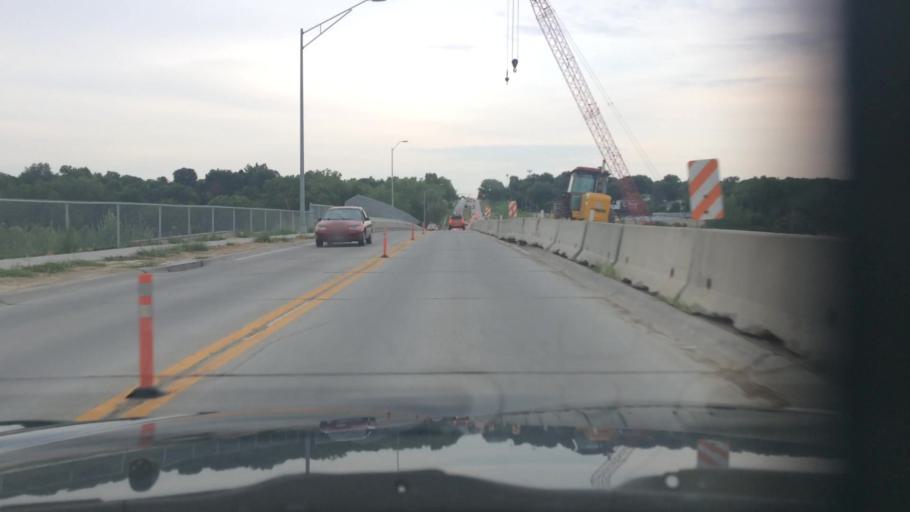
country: US
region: Nebraska
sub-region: Douglas County
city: Ralston
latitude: 41.1995
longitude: -96.0430
